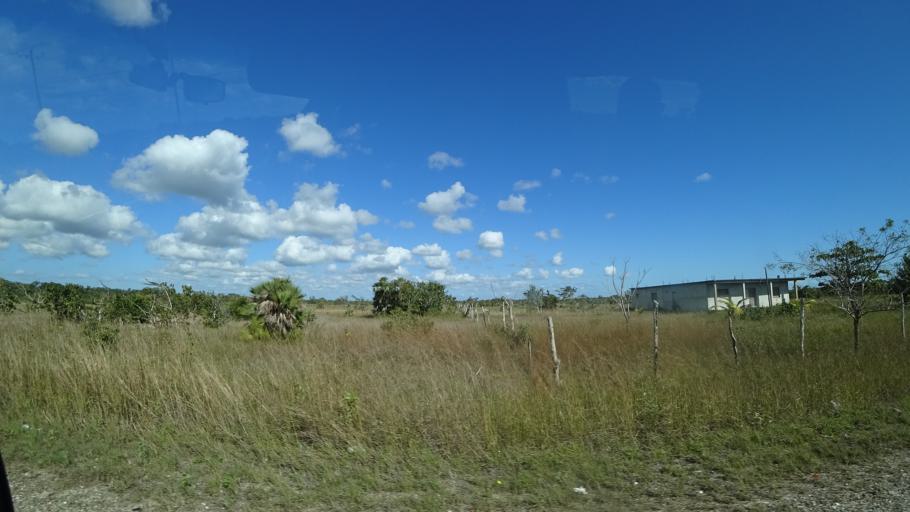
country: BZ
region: Belize
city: Belize City
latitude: 17.5806
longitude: -88.3797
